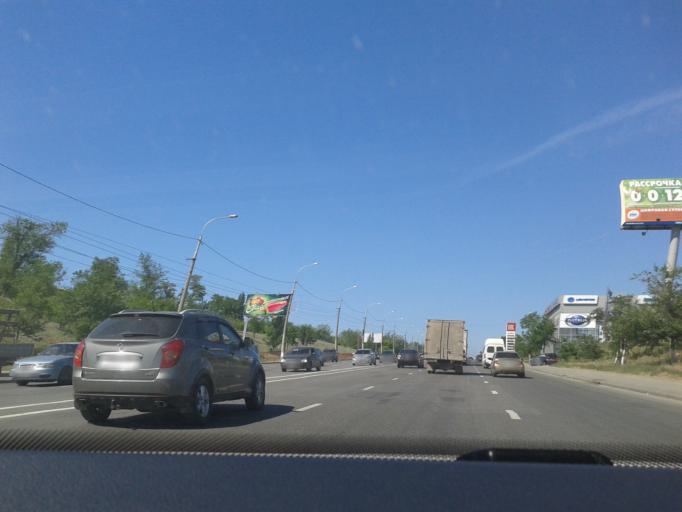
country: RU
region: Volgograd
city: Volgograd
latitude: 48.6677
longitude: 44.4414
